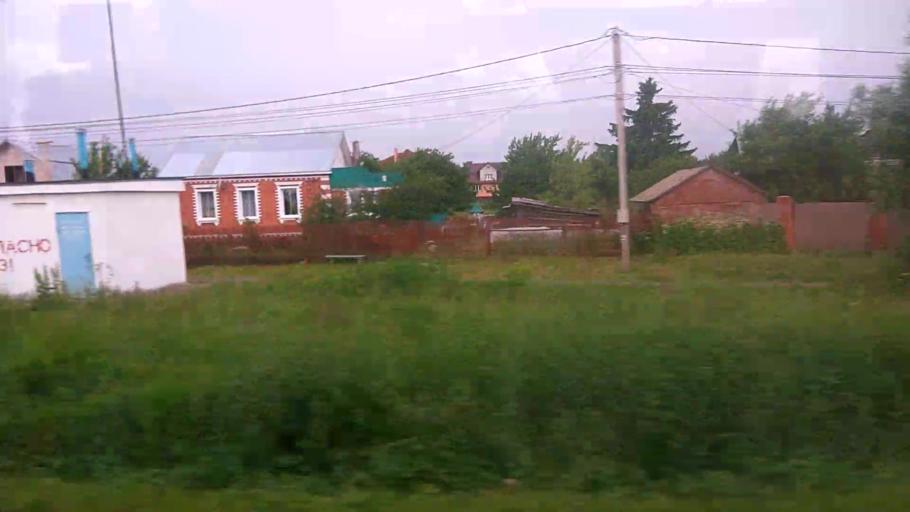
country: RU
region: Moskovskaya
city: Lukhovitsy
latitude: 54.9362
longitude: 39.0117
